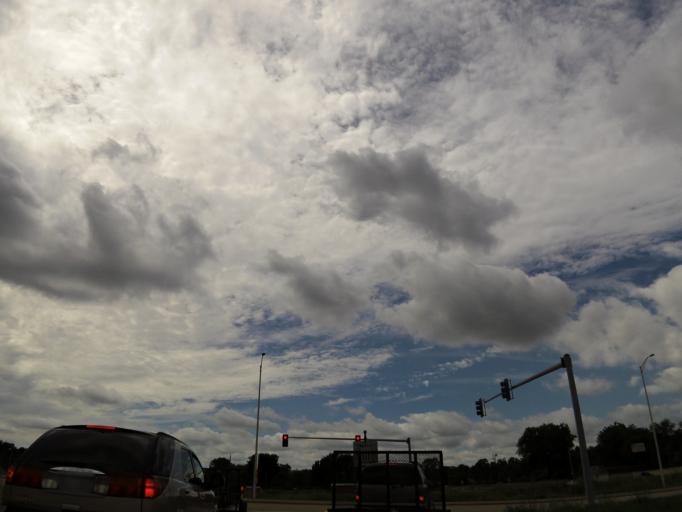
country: US
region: Illinois
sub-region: Saint Clair County
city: Washington Park
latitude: 38.6225
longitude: -90.0926
